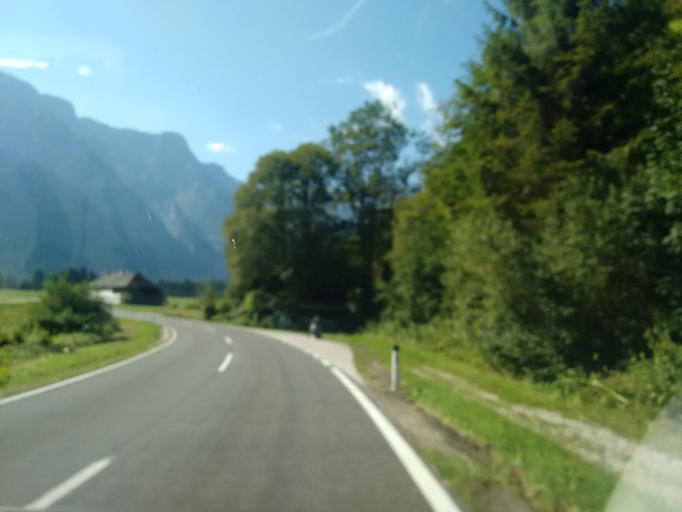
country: AT
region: Upper Austria
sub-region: Politischer Bezirk Gmunden
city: Gruenau im Almtal
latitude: 47.7473
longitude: 13.9504
